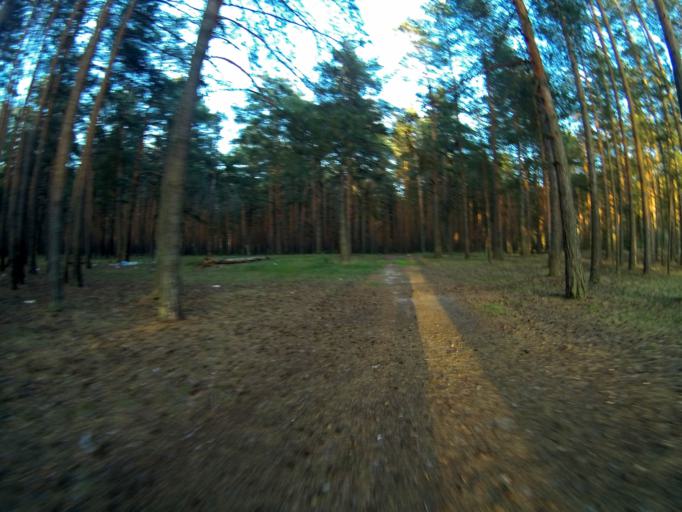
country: RU
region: Vladimir
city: Kommunar
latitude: 56.0980
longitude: 40.4462
